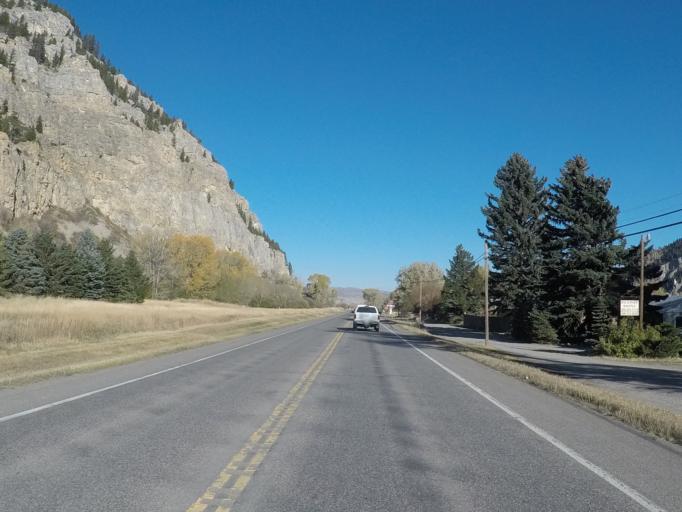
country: US
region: Montana
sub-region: Park County
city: Livingston
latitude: 45.6069
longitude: -110.5755
